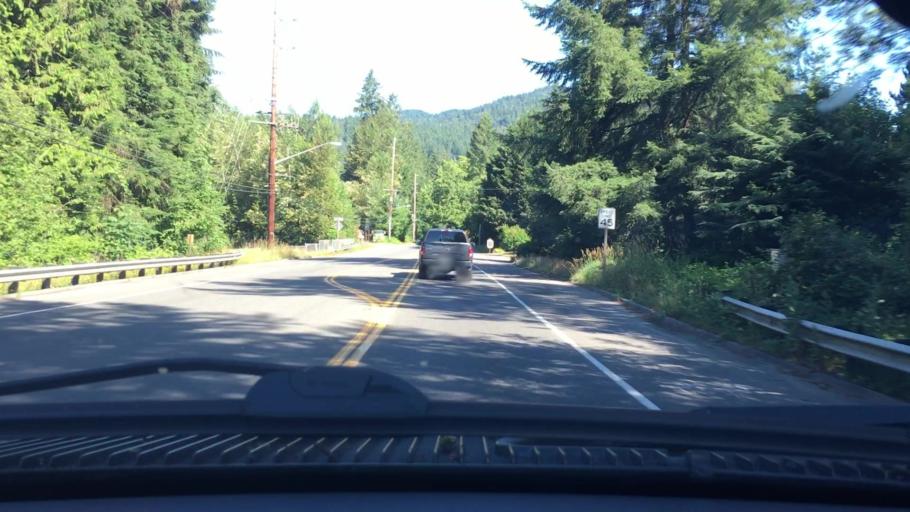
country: US
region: Washington
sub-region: King County
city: Mirrormont
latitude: 47.4760
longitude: -122.0265
